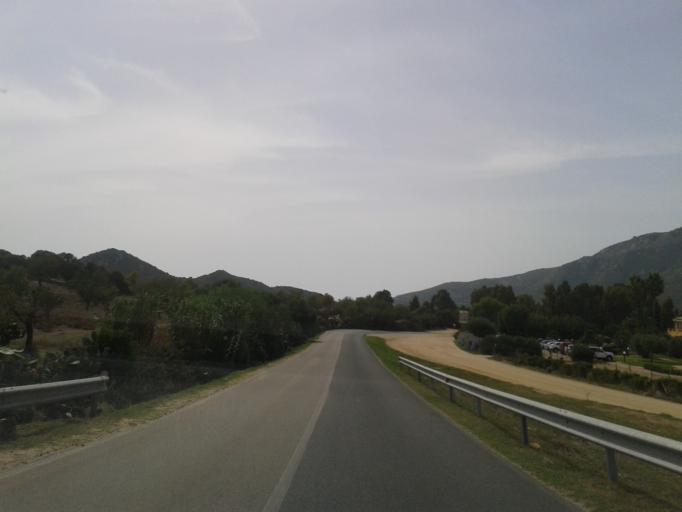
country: IT
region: Sardinia
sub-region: Provincia di Cagliari
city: Villasimius
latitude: 39.1456
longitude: 9.5057
